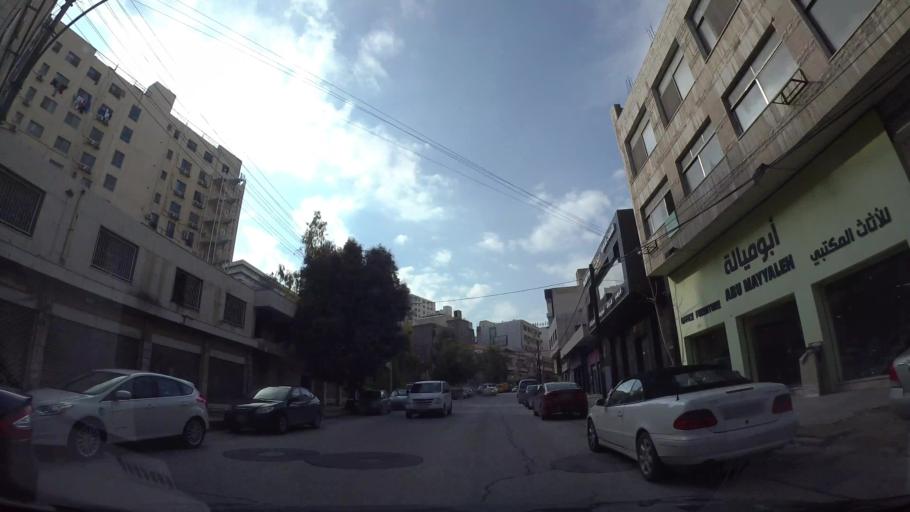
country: JO
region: Amman
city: Amman
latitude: 31.9549
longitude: 35.9169
